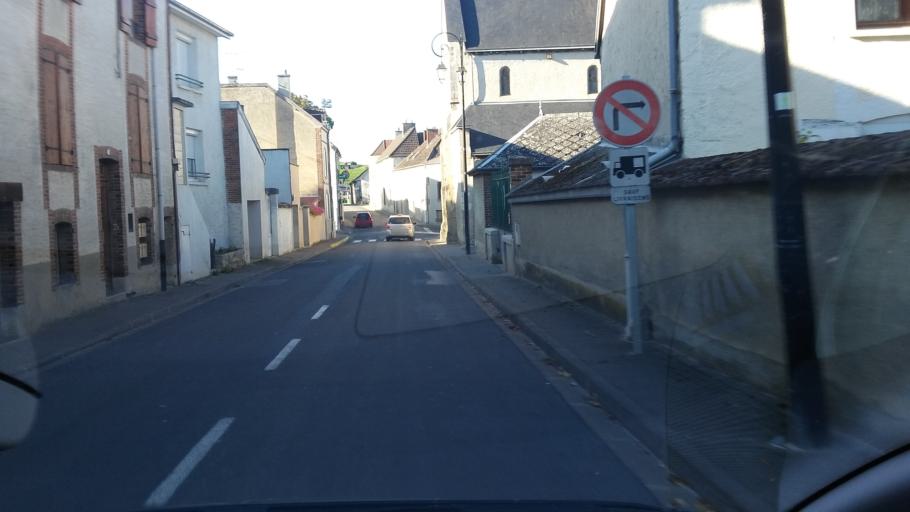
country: FR
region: Champagne-Ardenne
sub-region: Departement de la Marne
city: Avize
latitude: 48.9705
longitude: 4.0055
